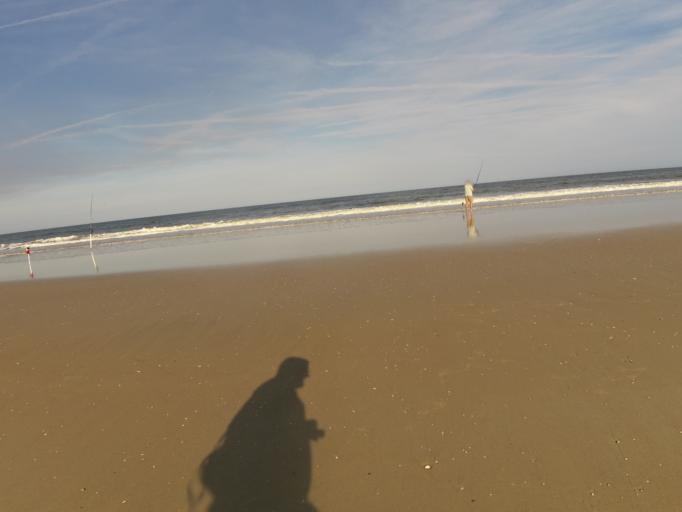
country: US
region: Florida
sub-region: Saint Johns County
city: Villano Beach
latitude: 29.9514
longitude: -81.3034
